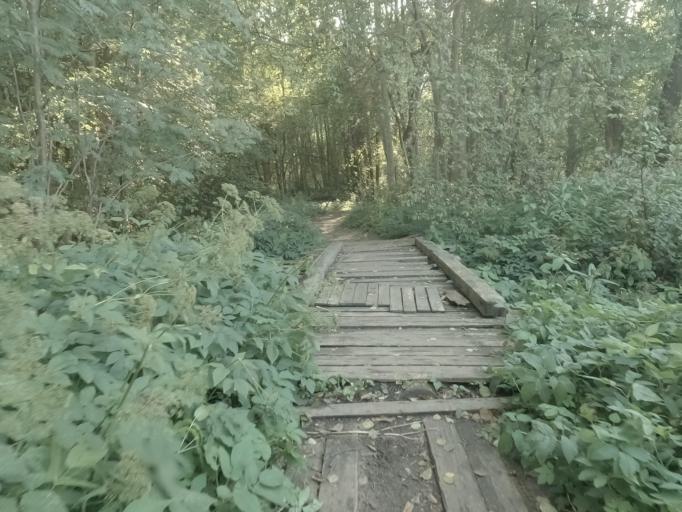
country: RU
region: Leningrad
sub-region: Volosovskiy Rayon
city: Shlissel'burg
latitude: 59.9463
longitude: 31.0052
